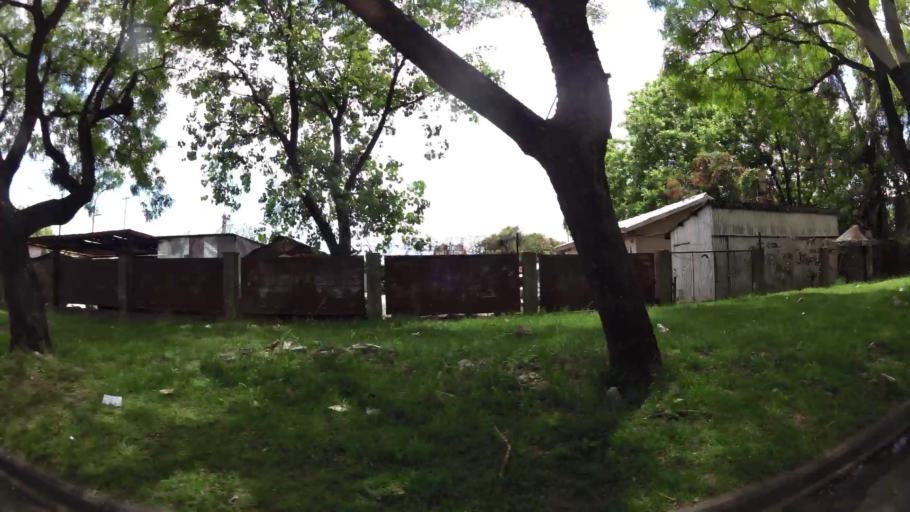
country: AR
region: Santa Fe
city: Gobernador Galvez
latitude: -32.9900
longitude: -60.6281
